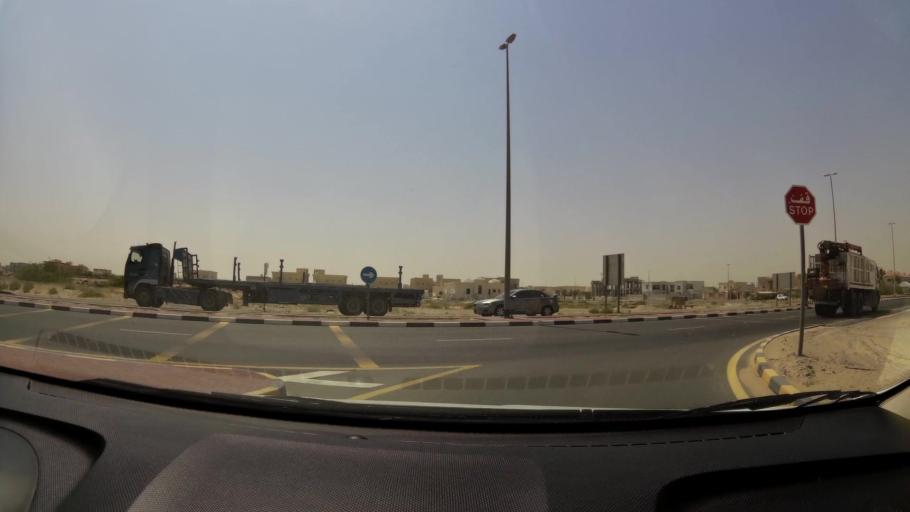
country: AE
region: Ajman
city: Ajman
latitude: 25.4140
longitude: 55.5277
